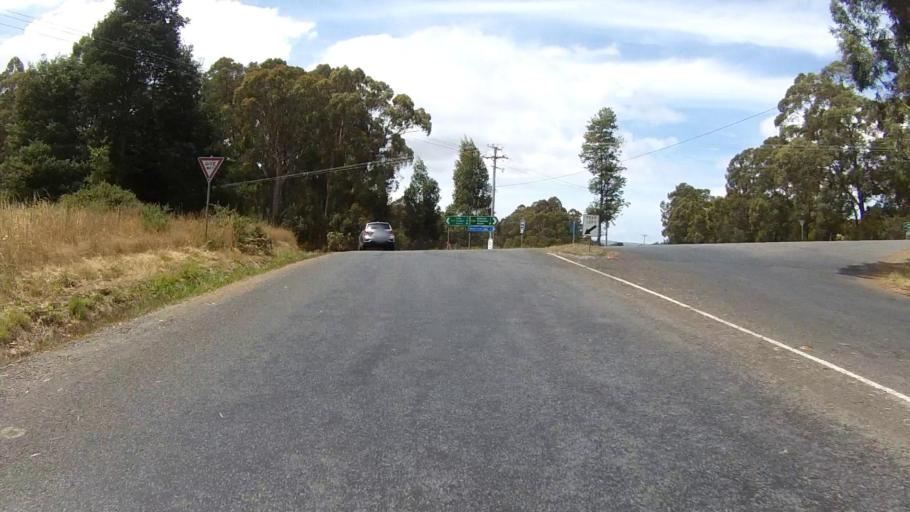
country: AU
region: Tasmania
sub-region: Kingborough
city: Kettering
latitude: -43.1062
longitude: 147.2436
